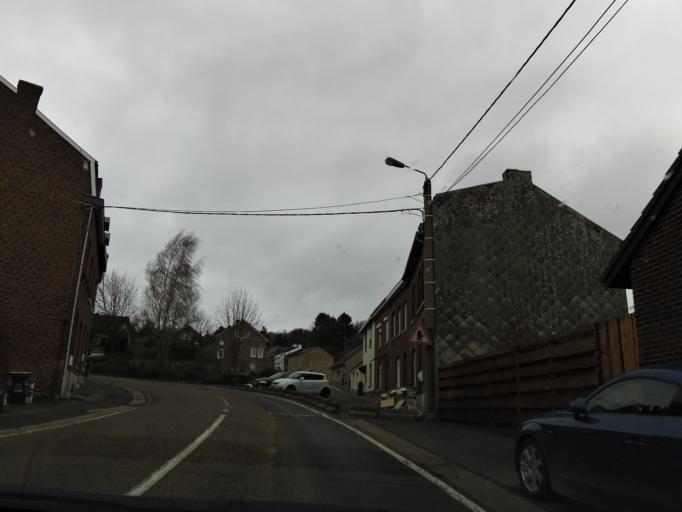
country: NL
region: Limburg
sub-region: Gemeente Vaals
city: Vaals
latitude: 50.7498
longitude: 6.0022
